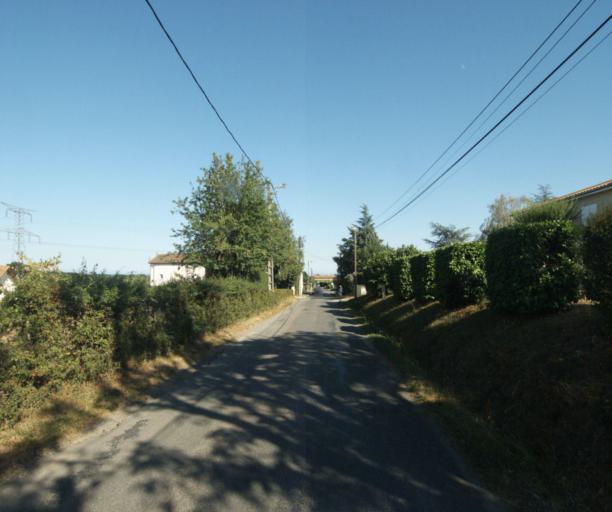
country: FR
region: Rhone-Alpes
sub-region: Departement du Rhone
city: Lentilly
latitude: 45.8082
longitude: 4.6816
